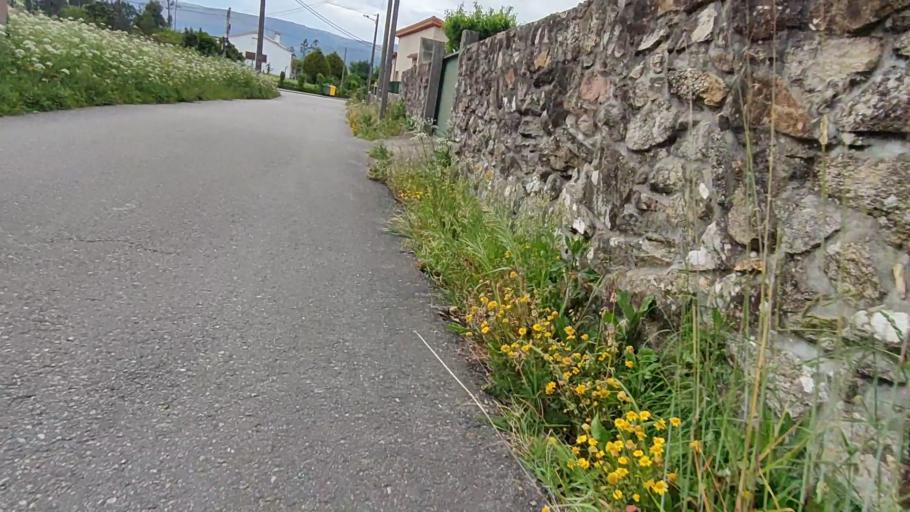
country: ES
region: Galicia
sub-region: Provincia da Coruna
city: Boiro
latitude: 42.6339
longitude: -8.8661
